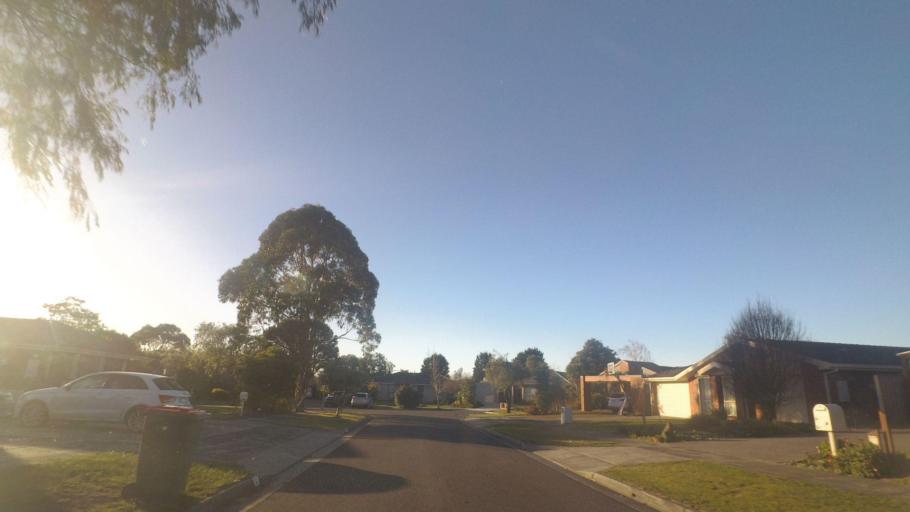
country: AU
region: Victoria
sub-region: Knox
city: Knoxfield
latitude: -37.9198
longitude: 145.2669
